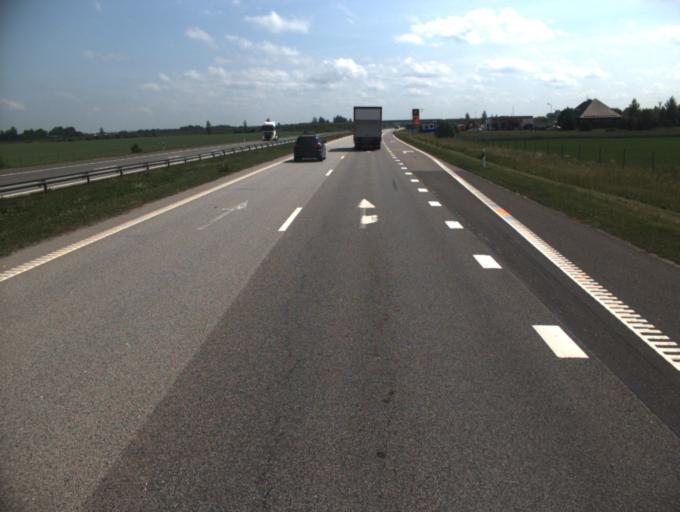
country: LT
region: Klaipedos apskritis
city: Gargzdai
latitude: 55.7325
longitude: 21.3717
